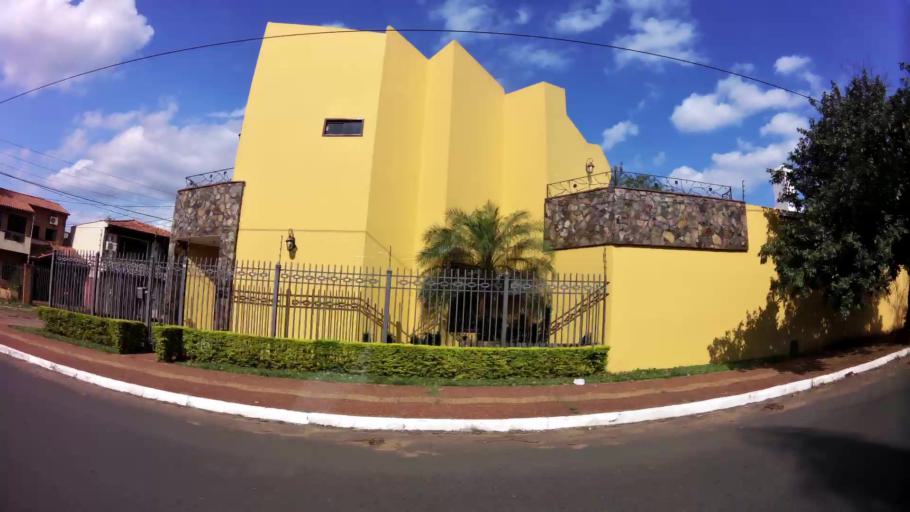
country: PY
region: Central
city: Fernando de la Mora
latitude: -25.3234
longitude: -57.5300
